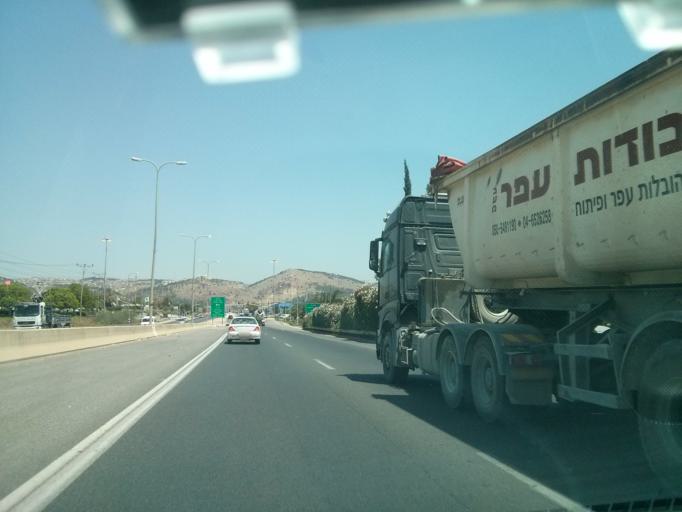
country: IL
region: Northern District
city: `Afula `Illit
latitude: 32.6465
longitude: 35.2916
